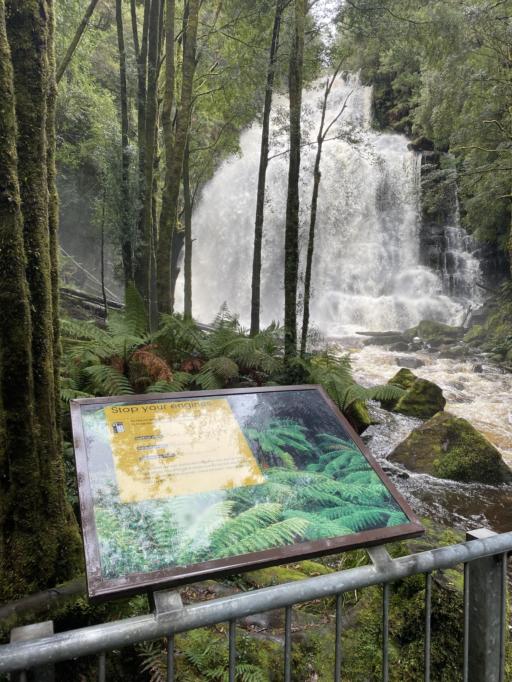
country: AU
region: Tasmania
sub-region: West Coast
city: Queenstown
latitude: -42.1006
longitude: 145.7376
